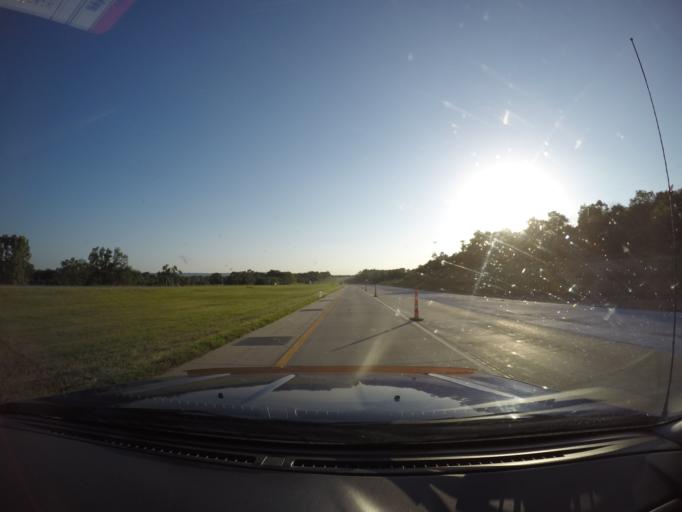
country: US
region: Kansas
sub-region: Riley County
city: Manhattan
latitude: 39.2007
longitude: -96.4415
